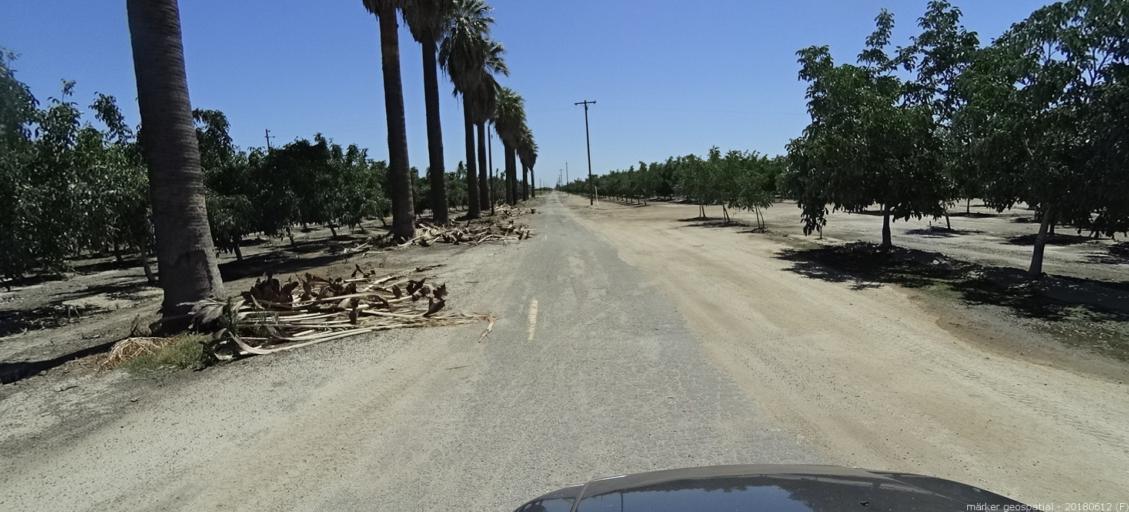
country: US
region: California
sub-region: Madera County
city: Chowchilla
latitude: 37.0472
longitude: -120.3202
